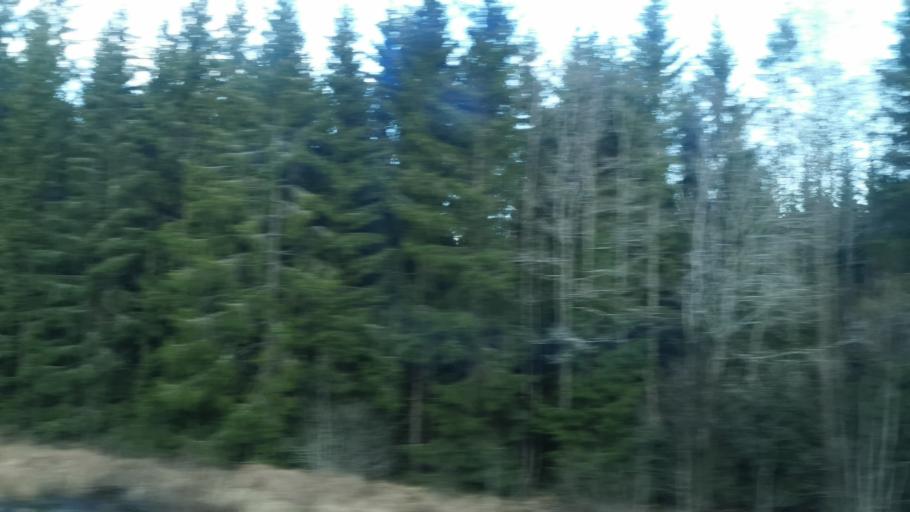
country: SE
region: Soedermanland
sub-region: Flens Kommun
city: Malmkoping
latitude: 59.0605
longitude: 16.6913
